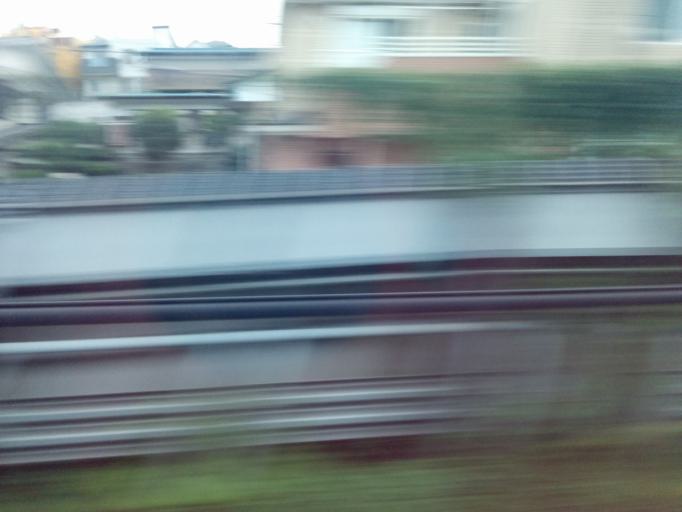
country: JP
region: Kanagawa
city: Yokohama
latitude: 35.4893
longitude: 139.5958
